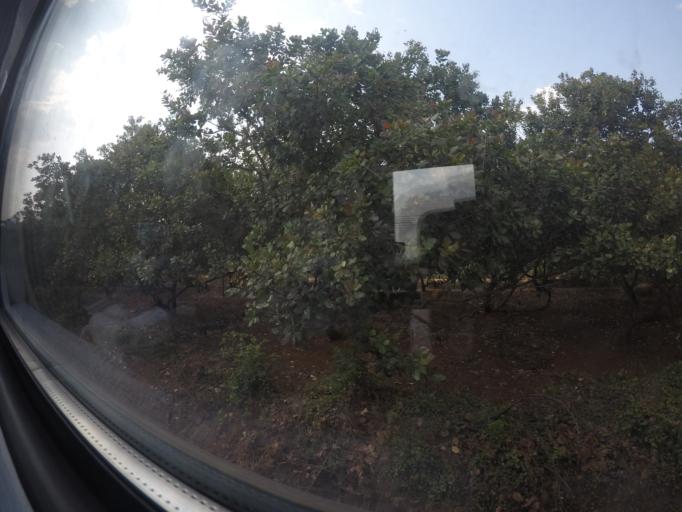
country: VN
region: Dong Nai
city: Thong Nhat
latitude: 10.9310
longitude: 107.1440
